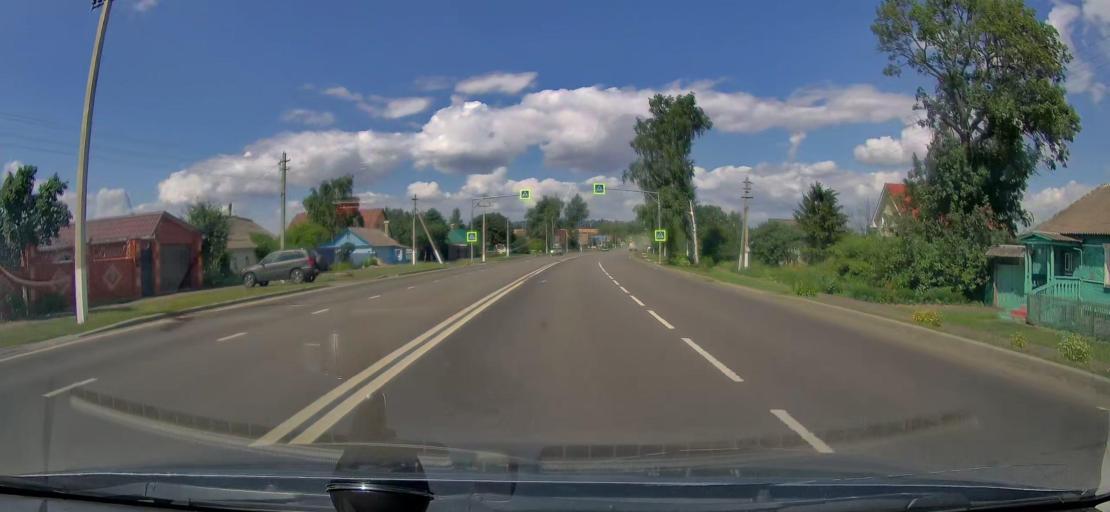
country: RU
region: Kursk
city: Zolotukhino
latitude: 51.9462
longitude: 36.3049
